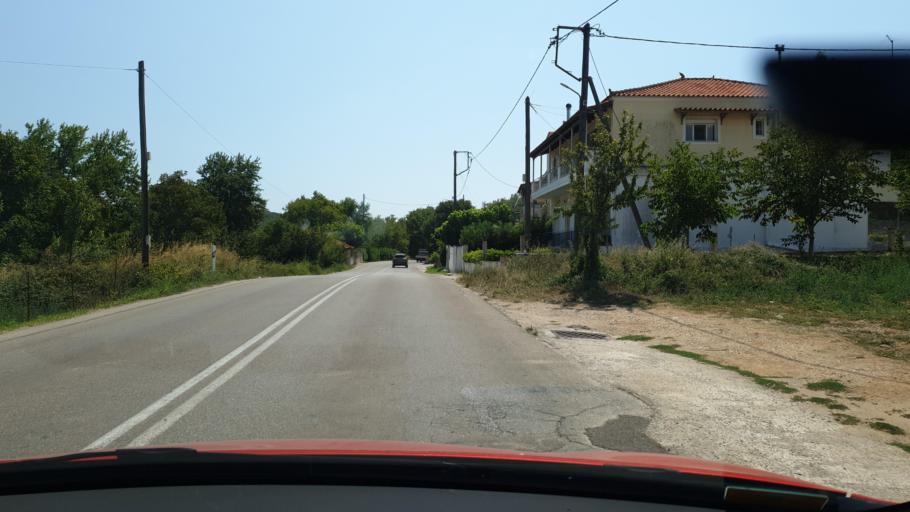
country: GR
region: Central Greece
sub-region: Nomos Evvoias
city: Aliveri
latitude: 38.4430
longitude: 24.1157
